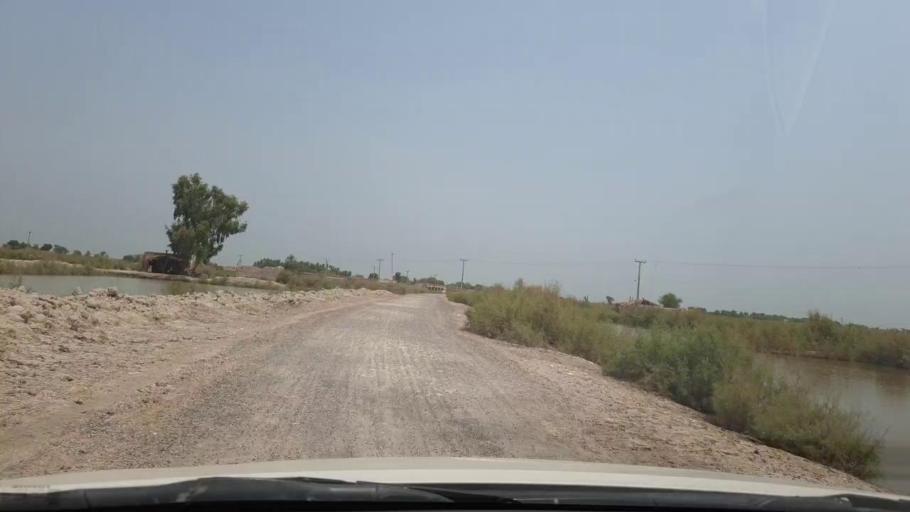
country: PK
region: Sindh
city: Rustam jo Goth
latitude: 28.0245
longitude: 68.7868
